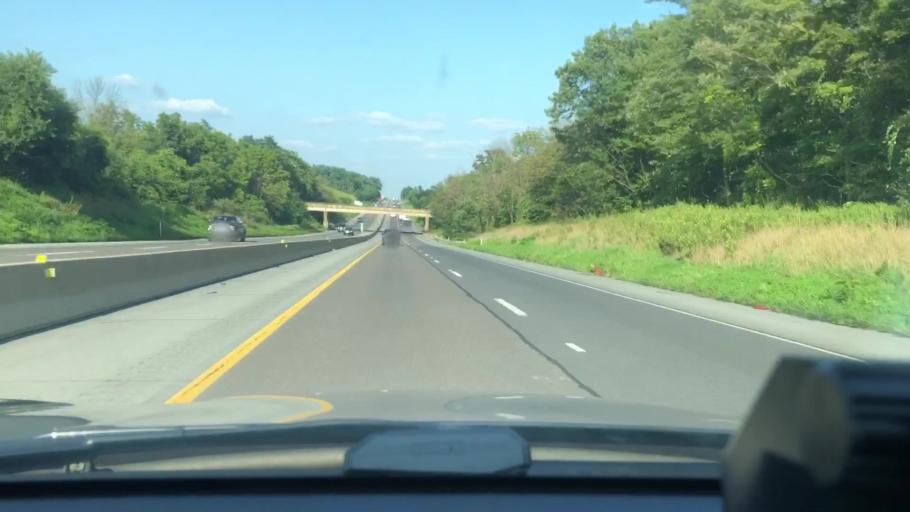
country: US
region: Pennsylvania
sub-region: Berks County
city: West Hamburg
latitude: 40.5261
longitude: -76.0804
